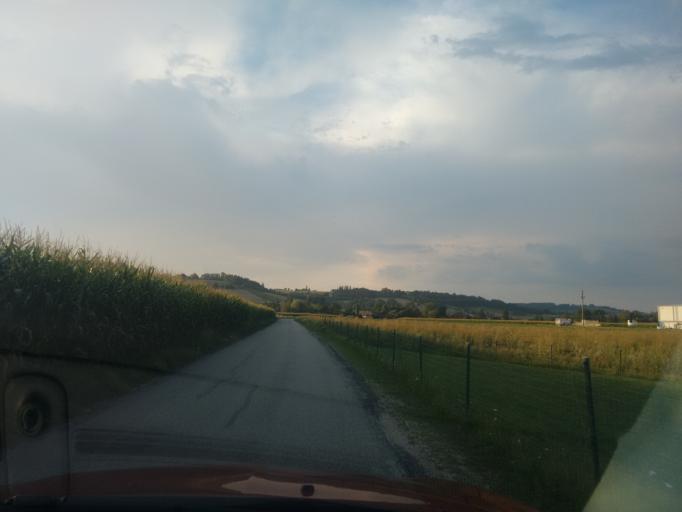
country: AT
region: Upper Austria
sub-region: Politischer Bezirk Grieskirchen
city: Bad Schallerbach
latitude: 48.2006
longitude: 13.9213
